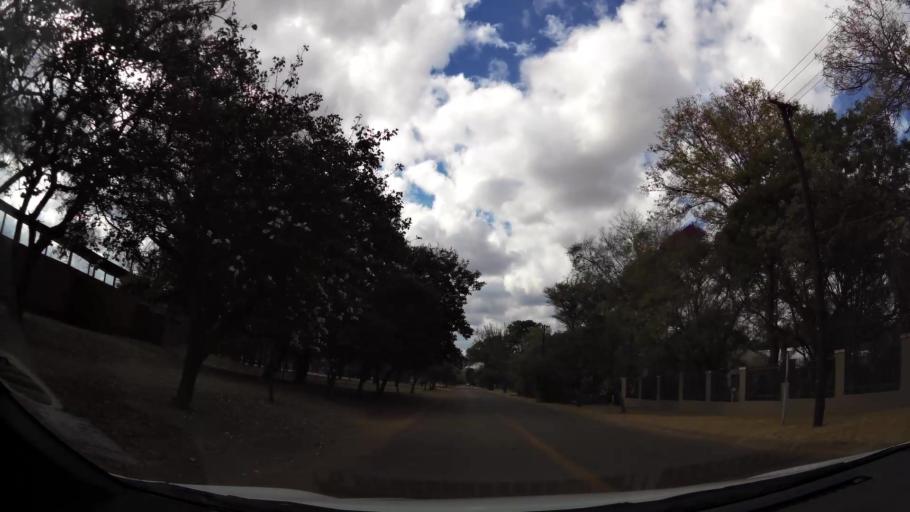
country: ZA
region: Limpopo
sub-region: Waterberg District Municipality
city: Modimolle
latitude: -24.7071
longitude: 28.4002
